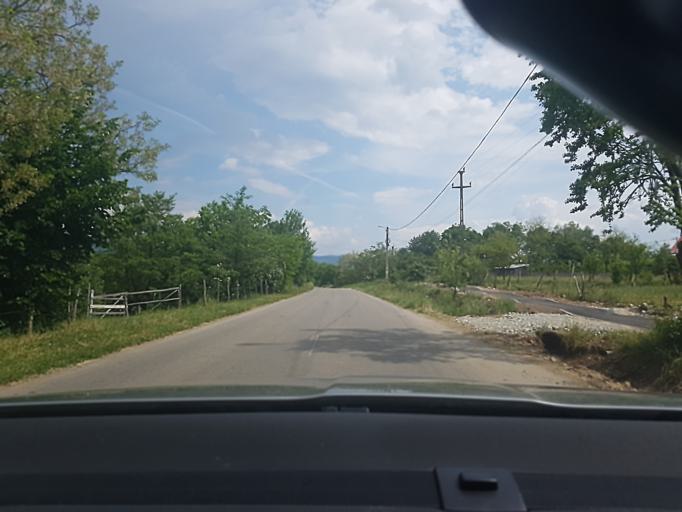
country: RO
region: Hunedoara
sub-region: Comuna Calan
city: Calan
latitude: 45.7216
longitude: 23.0250
